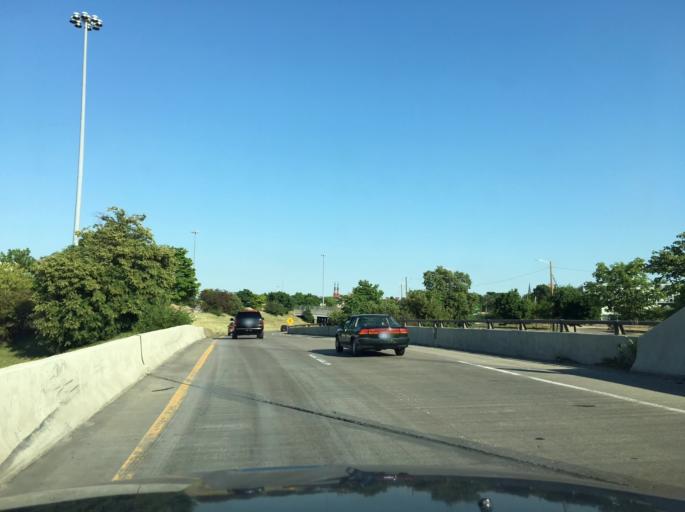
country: US
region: Michigan
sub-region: Wayne County
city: Hamtramck
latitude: 42.3665
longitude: -83.0595
